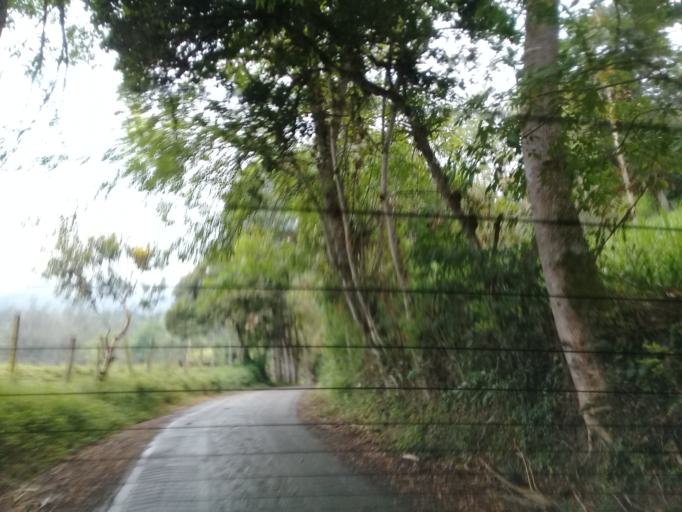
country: CO
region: Cundinamarca
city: Caqueza
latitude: 4.3942
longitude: -73.9809
